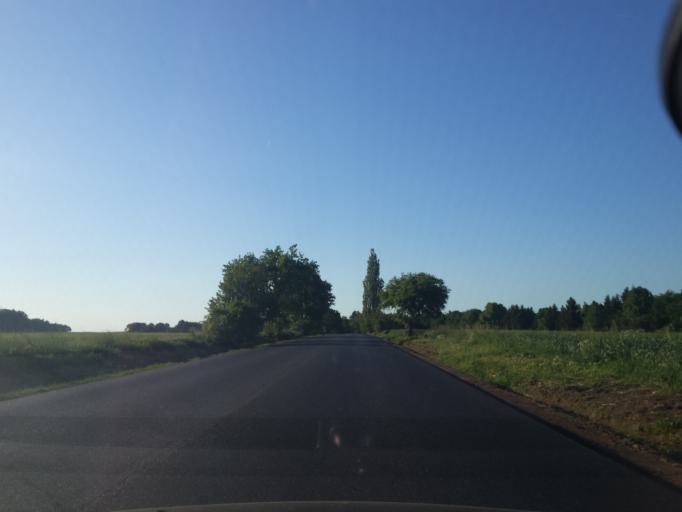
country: CZ
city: Duba
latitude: 50.5603
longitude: 14.5414
